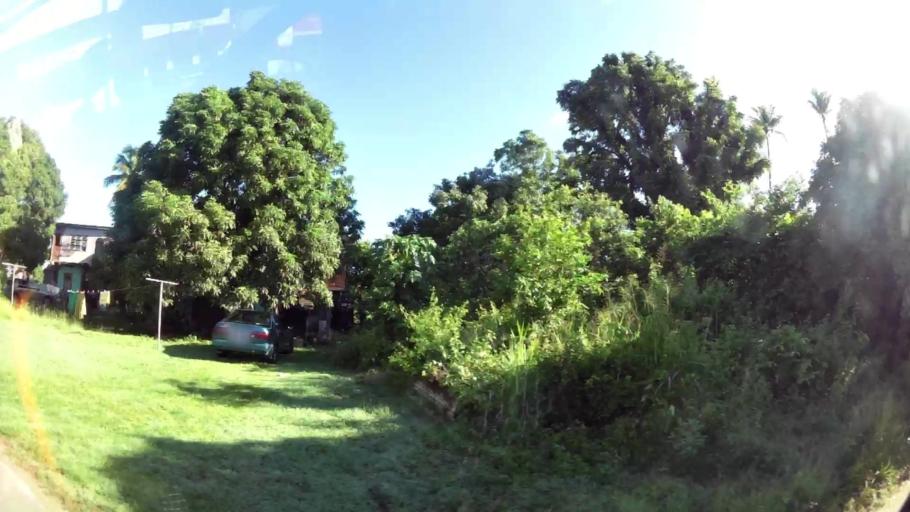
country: TT
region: Tobago
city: Scarborough
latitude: 11.1518
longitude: -60.8316
